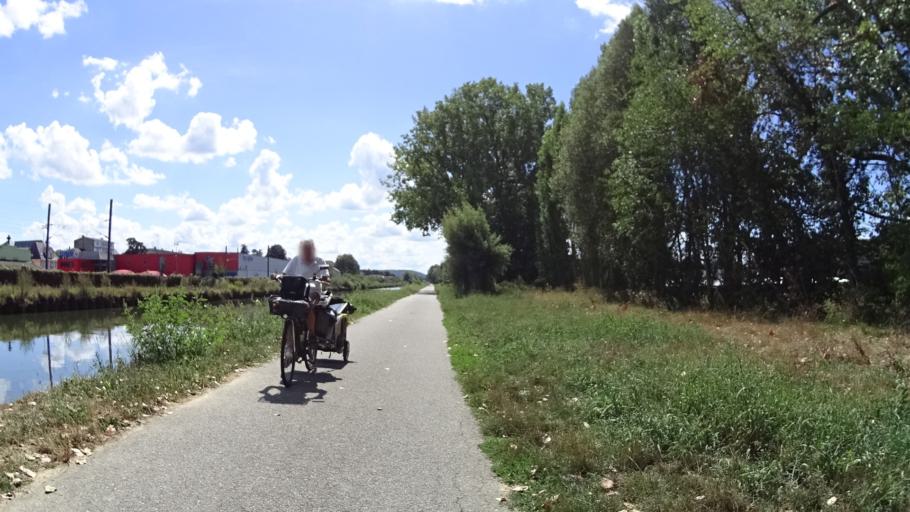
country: FR
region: Alsace
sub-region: Departement du Haut-Rhin
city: Brunstatt
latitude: 47.7277
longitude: 7.3205
